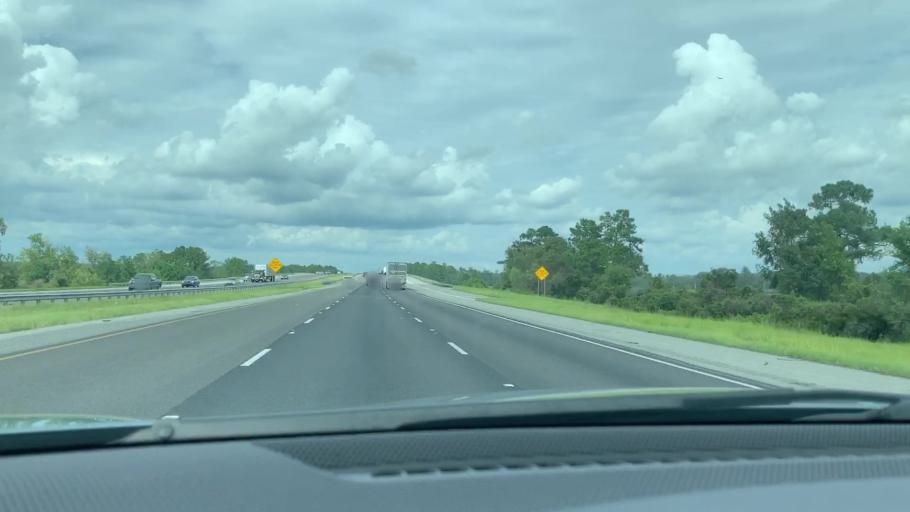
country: US
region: Georgia
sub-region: Liberty County
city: Midway
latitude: 31.7320
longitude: -81.3877
